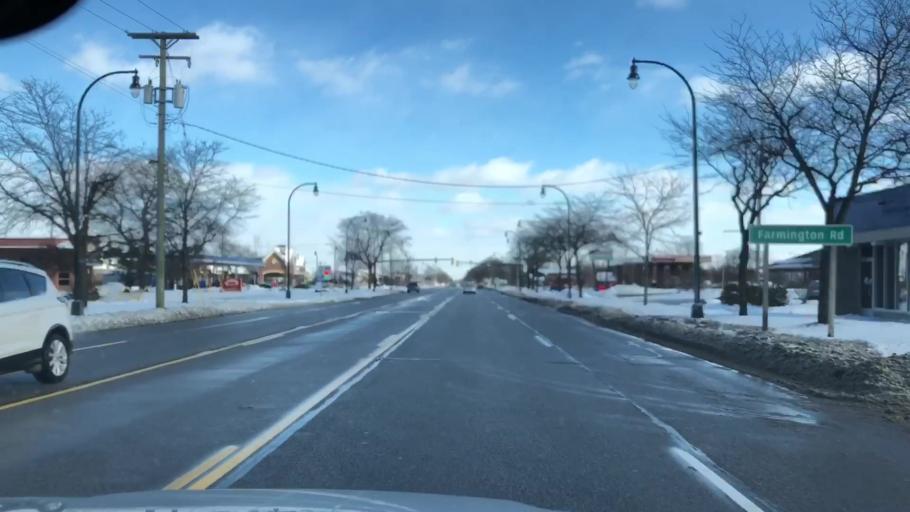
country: US
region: Michigan
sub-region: Wayne County
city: Livonia
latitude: 42.3682
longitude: -83.3743
